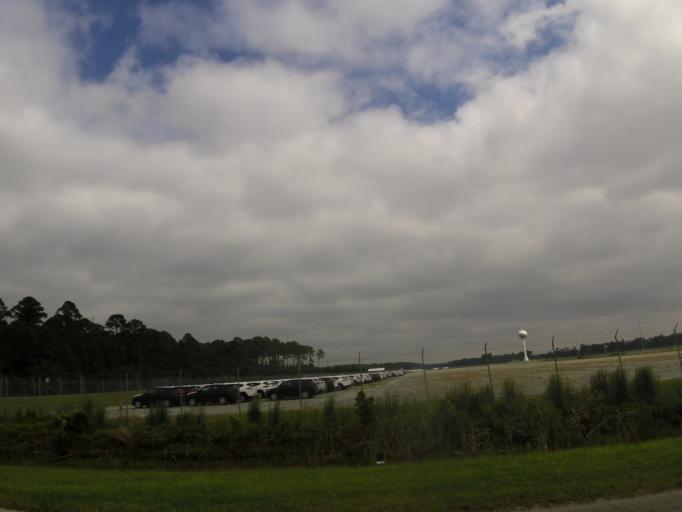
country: US
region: Georgia
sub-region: Glynn County
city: Brunswick
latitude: 31.1133
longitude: -81.5450
